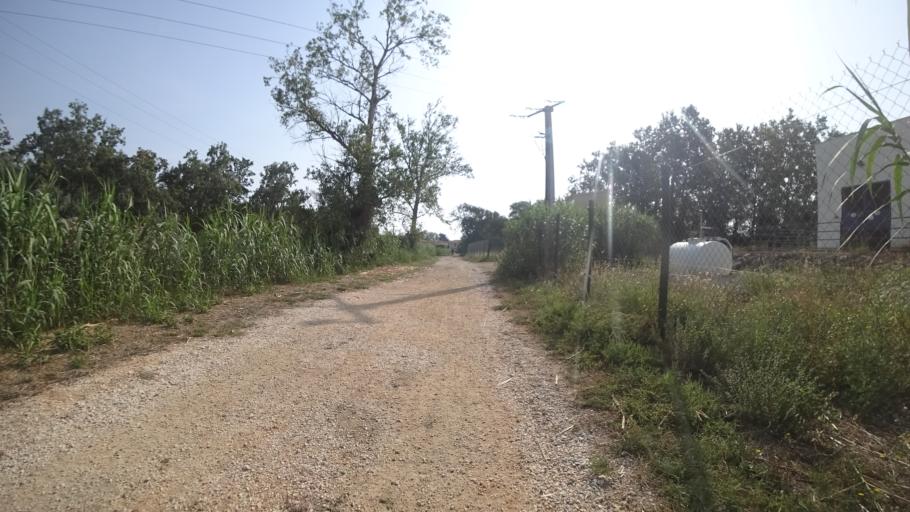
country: FR
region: Languedoc-Roussillon
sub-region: Departement des Pyrenees-Orientales
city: Sainte-Marie-Plage
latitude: 42.7386
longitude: 3.0291
